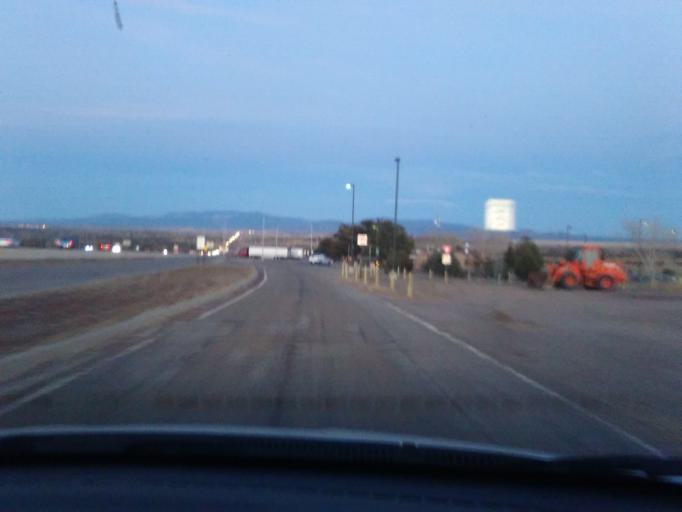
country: US
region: New Mexico
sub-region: Santa Fe County
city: La Cienega
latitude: 35.5269
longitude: -106.1576
